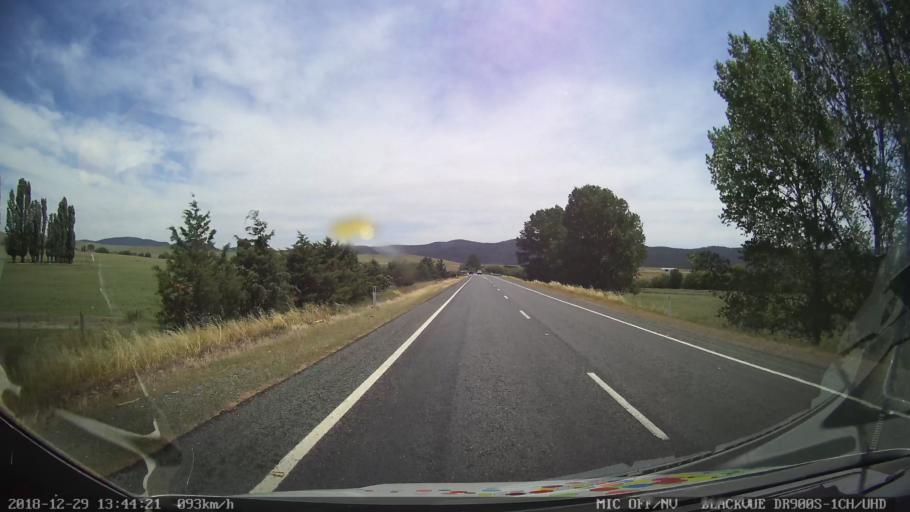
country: AU
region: New South Wales
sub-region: Cooma-Monaro
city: Cooma
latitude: -36.0832
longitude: 149.1536
